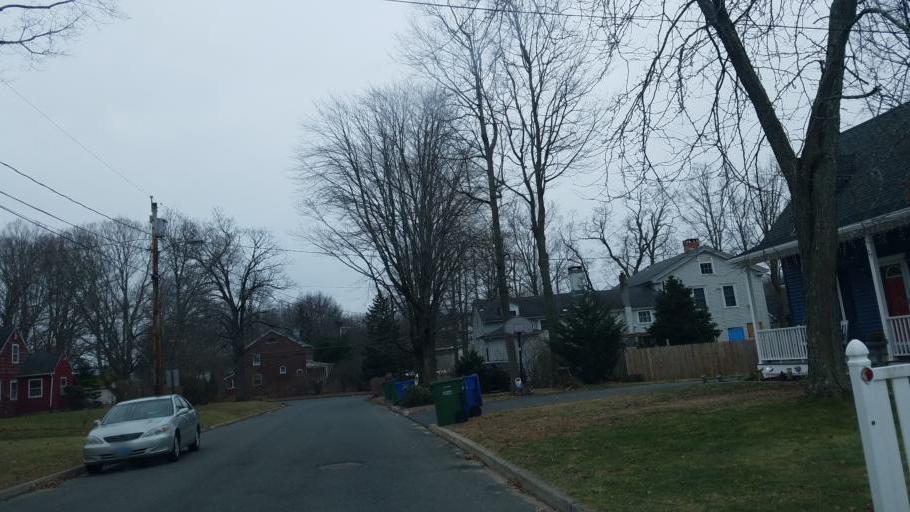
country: US
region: Connecticut
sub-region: Middlesex County
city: Middletown
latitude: 41.5476
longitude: -72.6333
